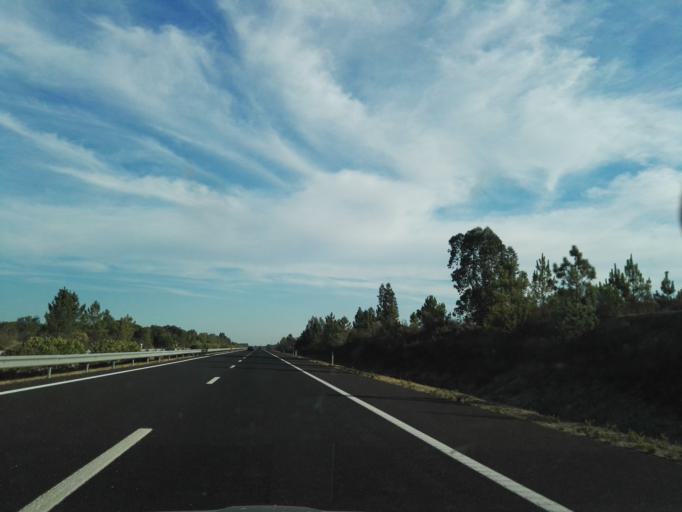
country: PT
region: Santarem
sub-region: Benavente
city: Poceirao
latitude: 38.8065
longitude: -8.7024
